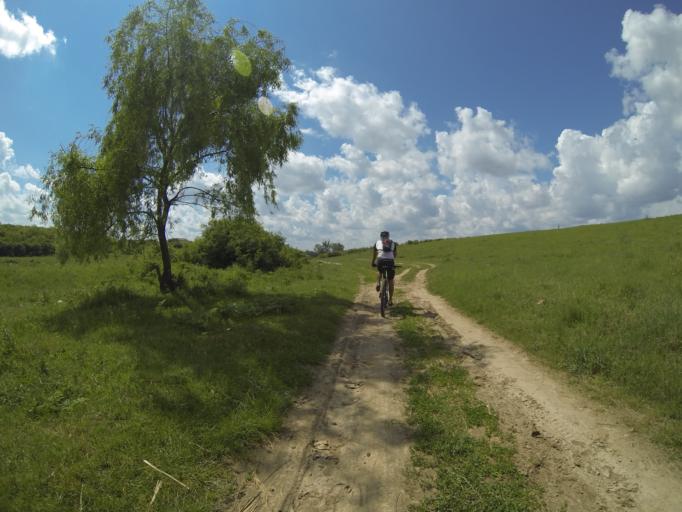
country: RO
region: Dolj
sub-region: Comuna Malu Mare
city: Preajba
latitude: 44.2645
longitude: 23.8654
